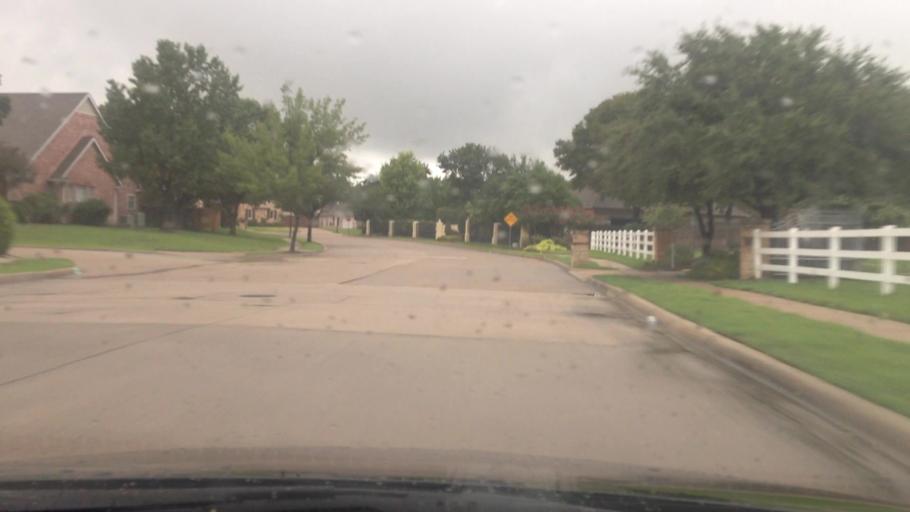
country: US
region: Texas
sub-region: Tarrant County
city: Colleyville
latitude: 32.8846
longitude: -97.1760
